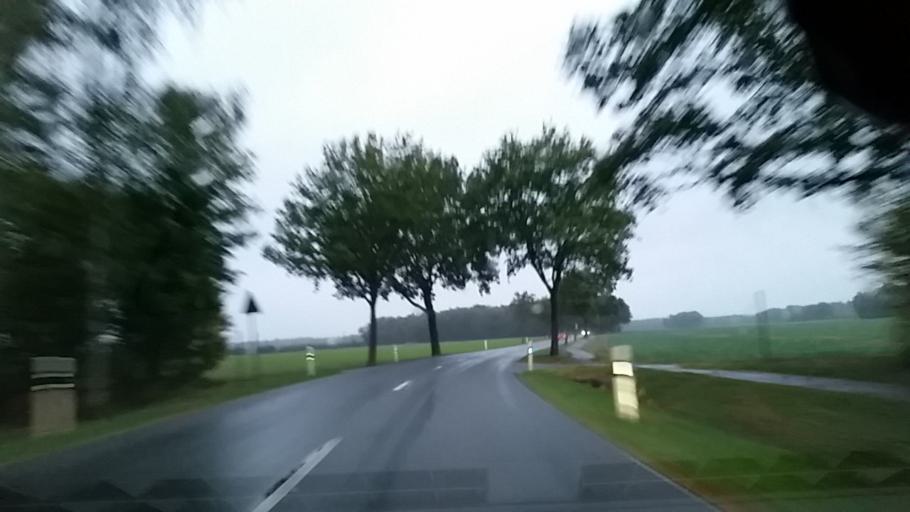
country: DE
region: Lower Saxony
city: Weyhausen
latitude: 52.4795
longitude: 10.7162
